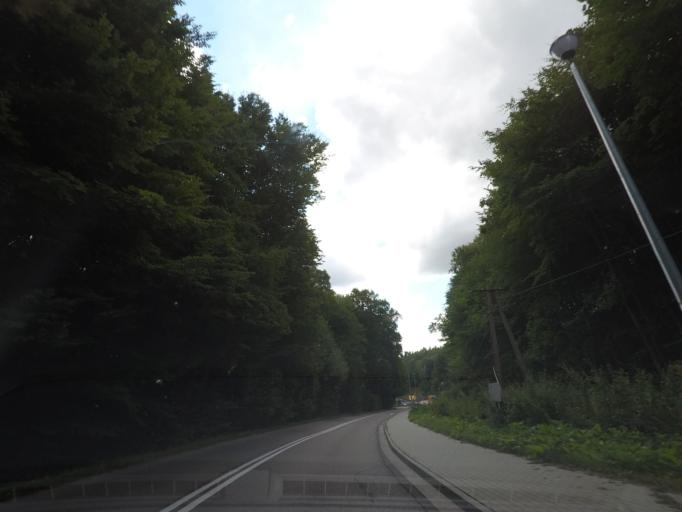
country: PL
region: Pomeranian Voivodeship
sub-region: Powiat wejherowski
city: Leczyce
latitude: 54.5972
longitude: 17.8482
